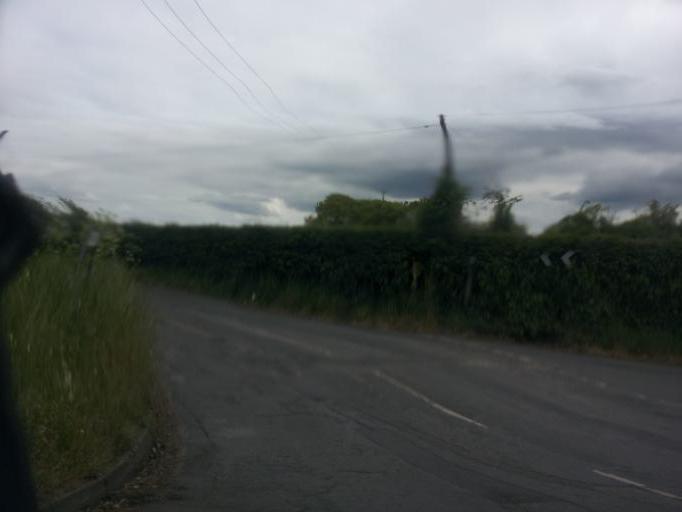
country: GB
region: England
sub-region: Kent
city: Newington
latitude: 51.3741
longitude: 0.6716
